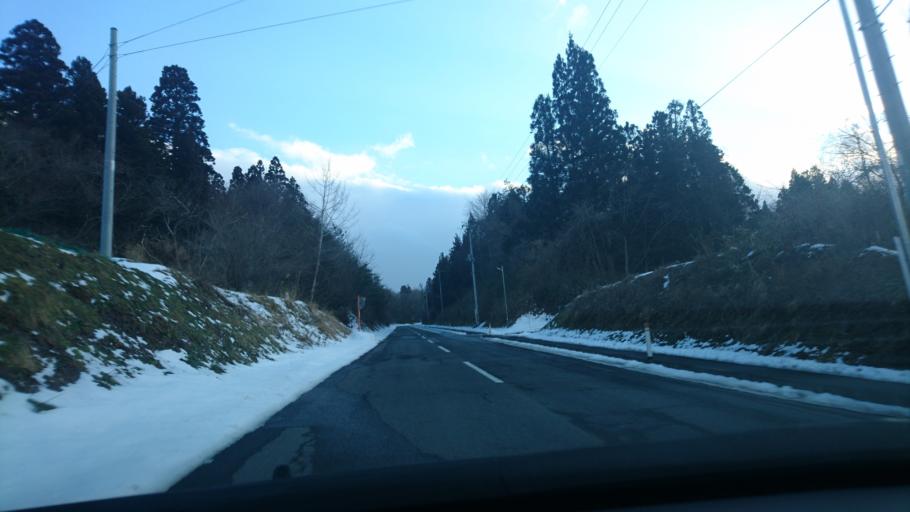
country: JP
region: Iwate
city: Ichinoseki
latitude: 39.0150
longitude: 141.3393
